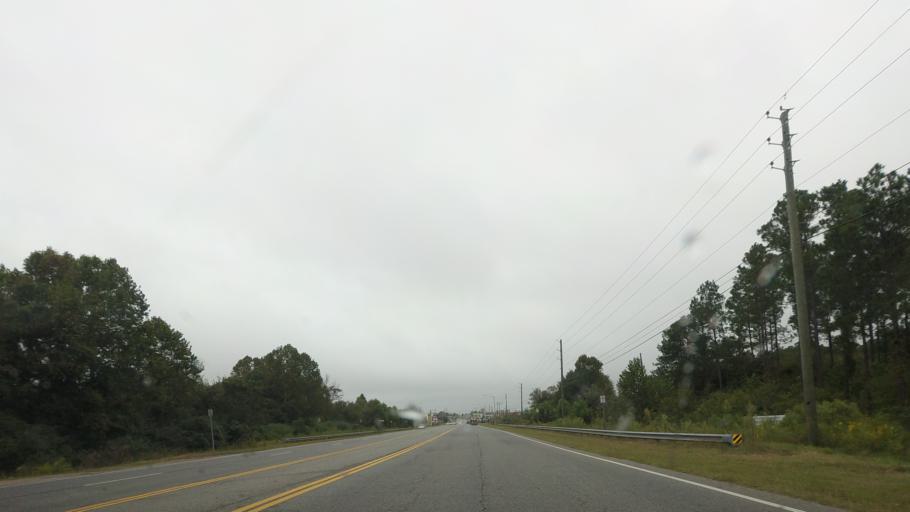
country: US
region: Georgia
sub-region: Ben Hill County
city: Fitzgerald
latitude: 31.6904
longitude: -83.2434
